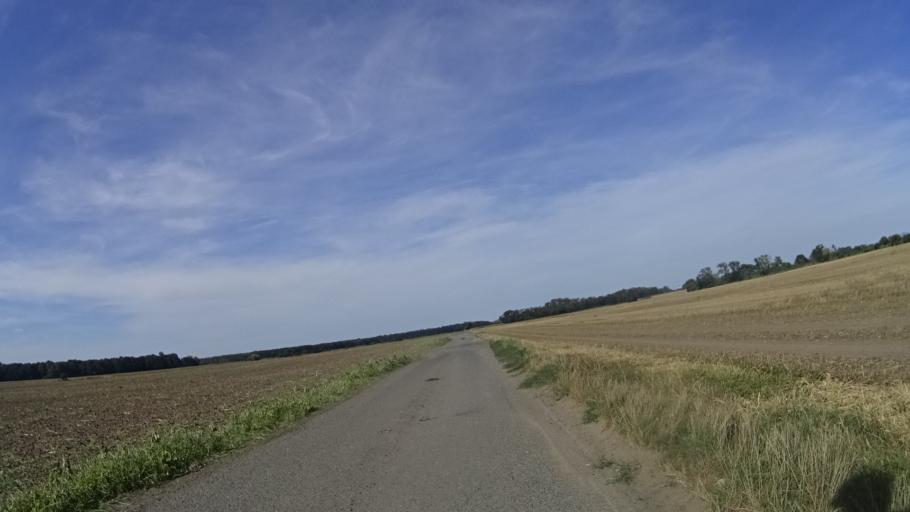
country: AT
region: Lower Austria
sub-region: Politischer Bezirk Ganserndorf
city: Durnkrut
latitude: 48.4419
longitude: 16.8773
